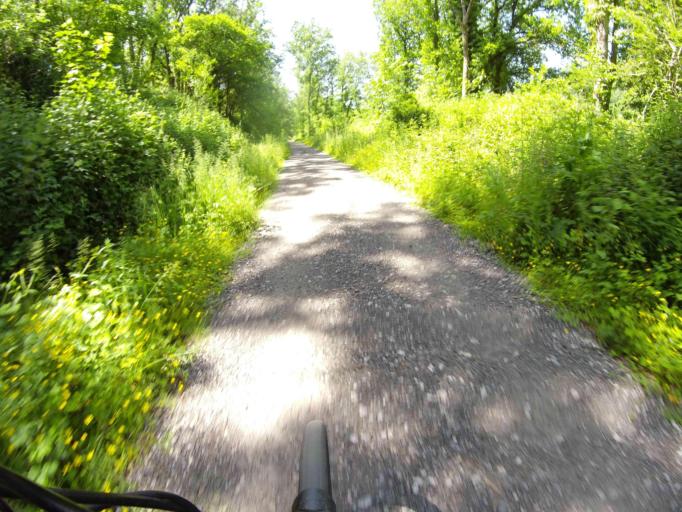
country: GB
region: England
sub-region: Devon
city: Bovey Tracey
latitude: 50.6278
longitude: -3.7197
